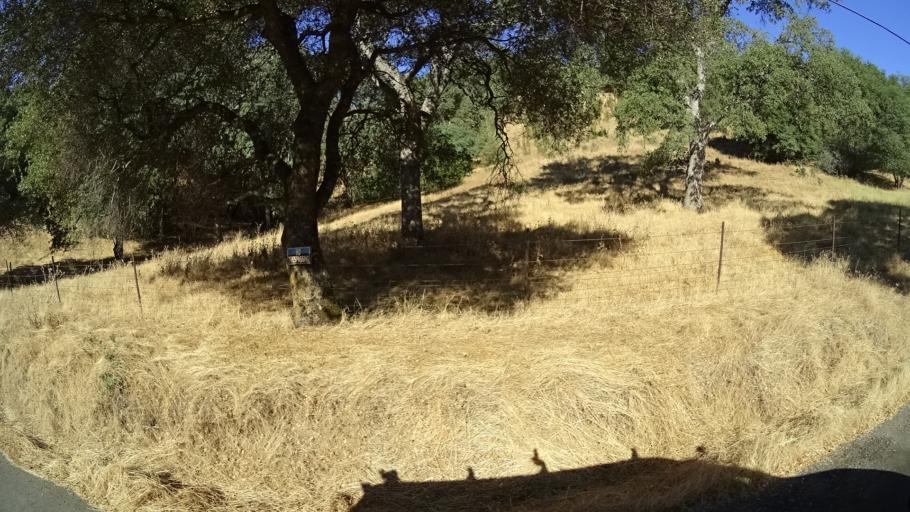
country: US
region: California
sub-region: Calaveras County
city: Angels Camp
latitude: 38.0420
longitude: -120.5064
